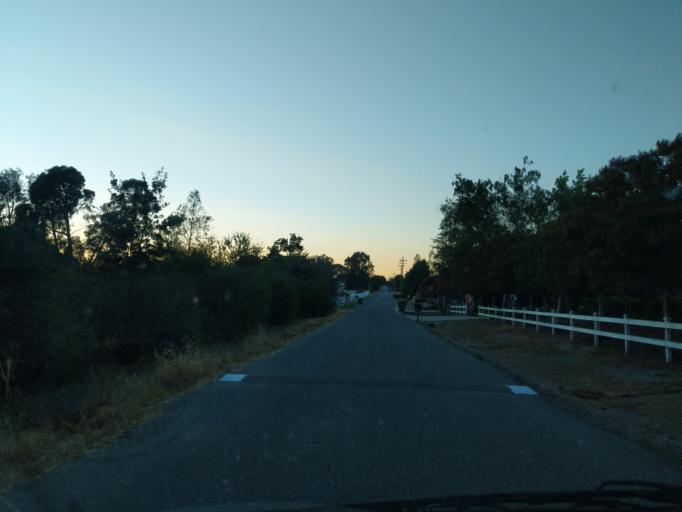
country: US
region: California
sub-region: Santa Clara County
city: Gilroy
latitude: 37.0602
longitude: -121.5573
